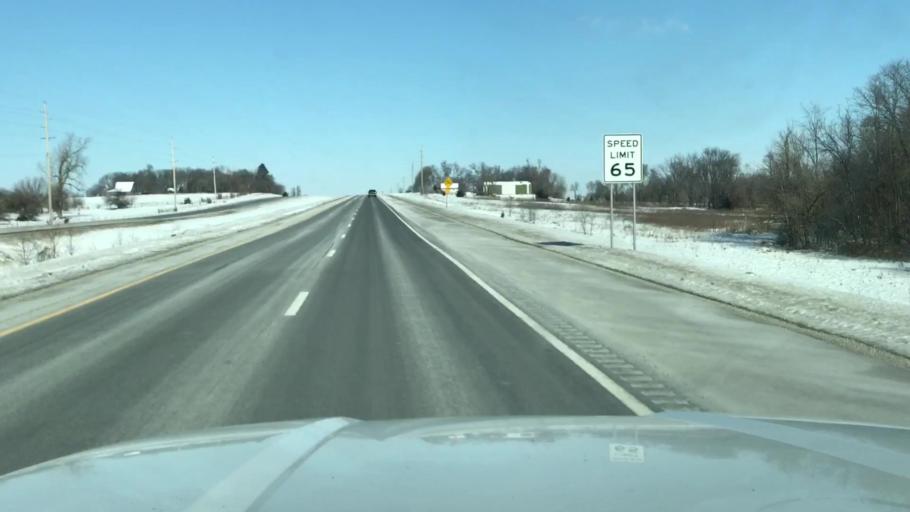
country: US
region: Missouri
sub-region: Nodaway County
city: Maryville
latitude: 40.2013
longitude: -94.8676
